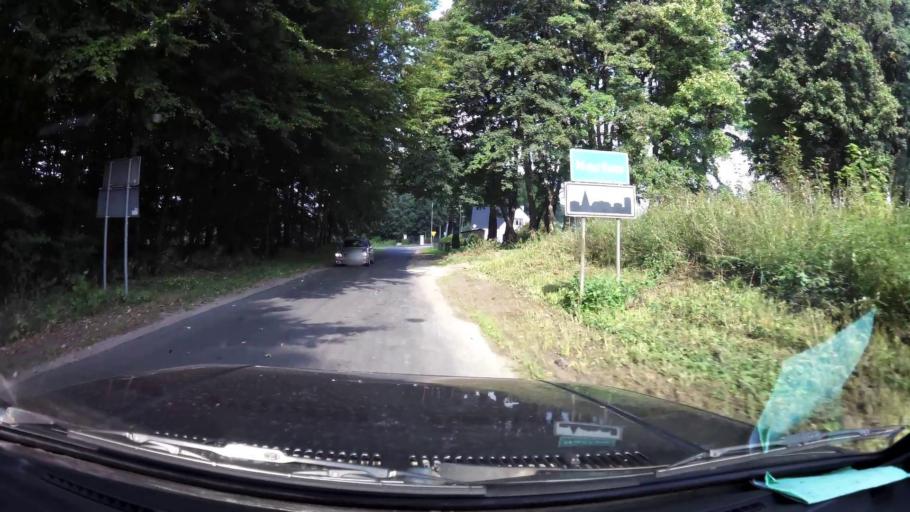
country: PL
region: West Pomeranian Voivodeship
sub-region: Powiat koszalinski
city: Polanow
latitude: 54.1378
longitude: 16.5226
